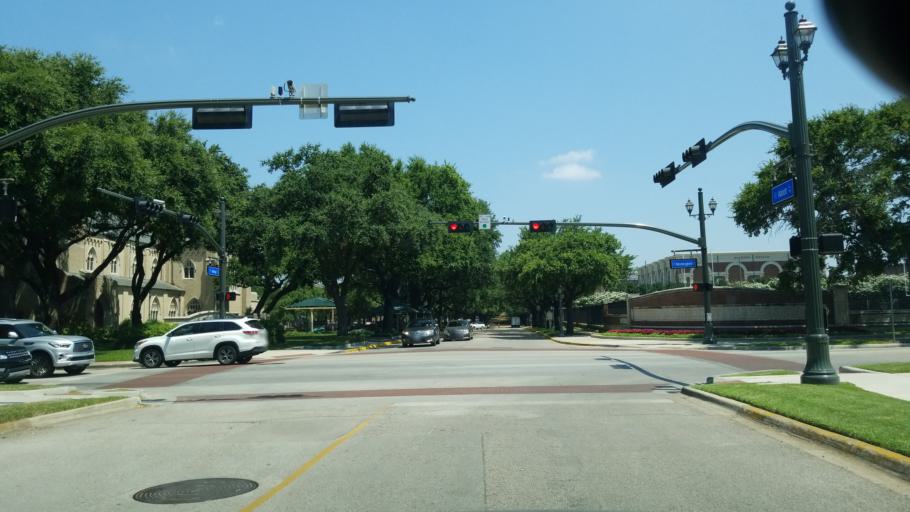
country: US
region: Texas
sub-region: Dallas County
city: Highland Park
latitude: 32.8363
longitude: -96.7852
